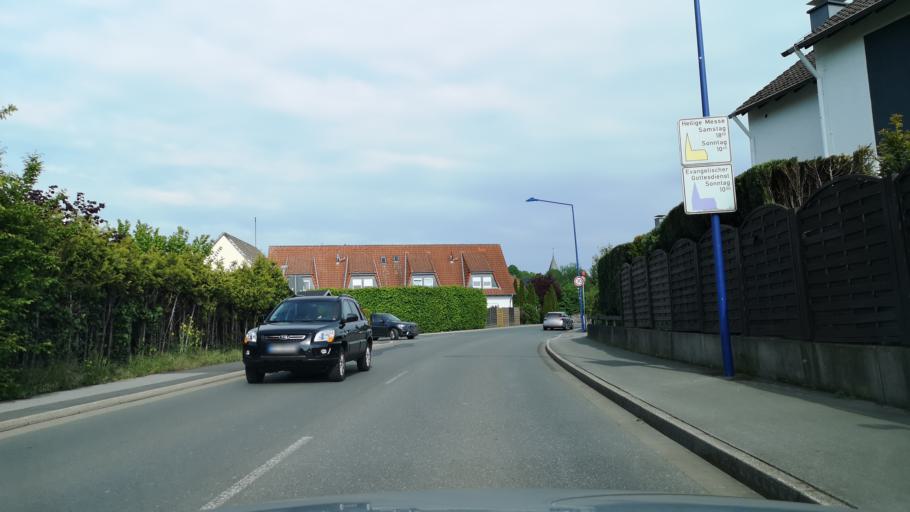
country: DE
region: North Rhine-Westphalia
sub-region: Regierungsbezirk Arnsberg
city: Holzwickede
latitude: 51.4455
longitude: 7.6454
